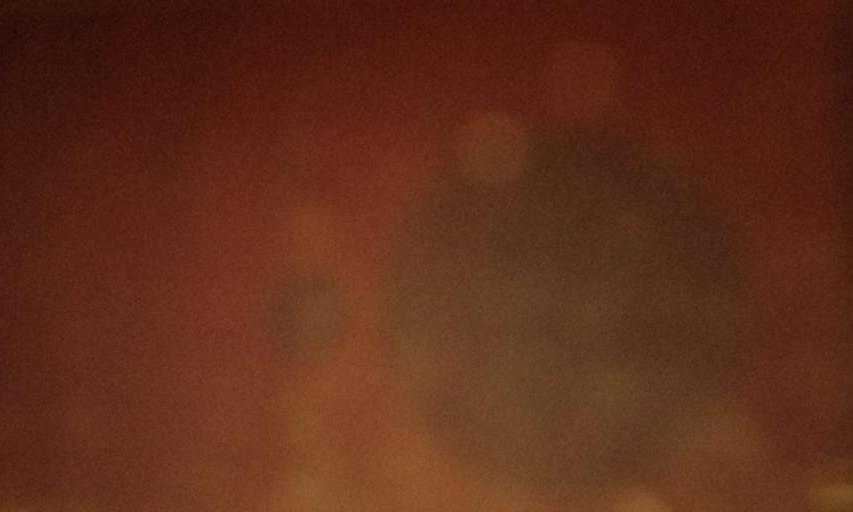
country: JP
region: Hiroshima
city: Mihara
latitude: 34.3988
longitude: 133.0544
